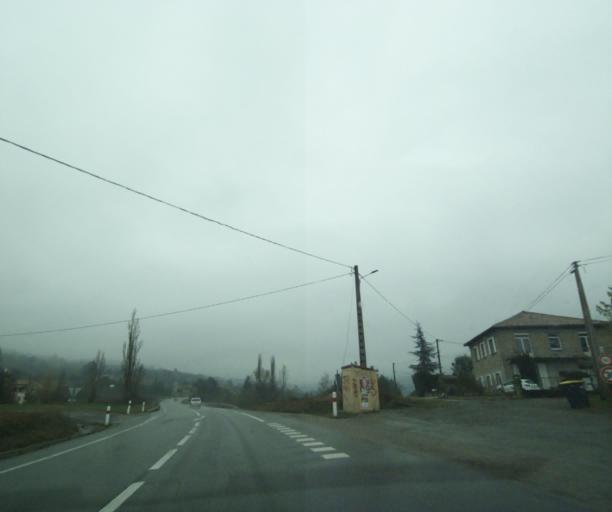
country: FR
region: Rhone-Alpes
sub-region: Departement de l'Ardeche
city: Vesseaux
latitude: 44.6584
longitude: 4.4491
